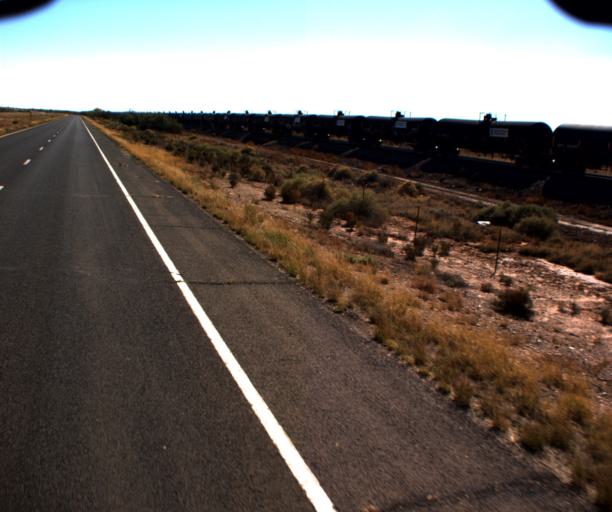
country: US
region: Arizona
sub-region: Navajo County
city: Winslow
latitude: 35.0108
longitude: -110.6687
